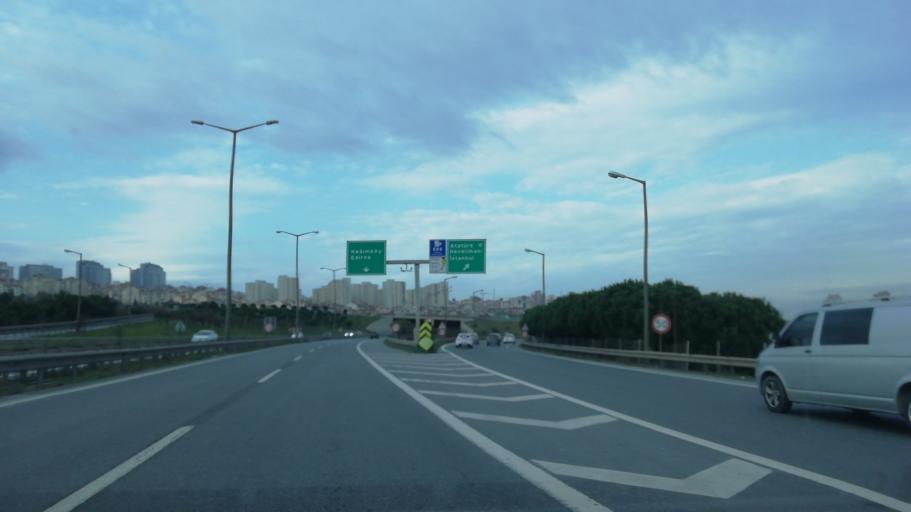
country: TR
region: Istanbul
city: Esenyurt
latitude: 41.0525
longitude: 28.6842
